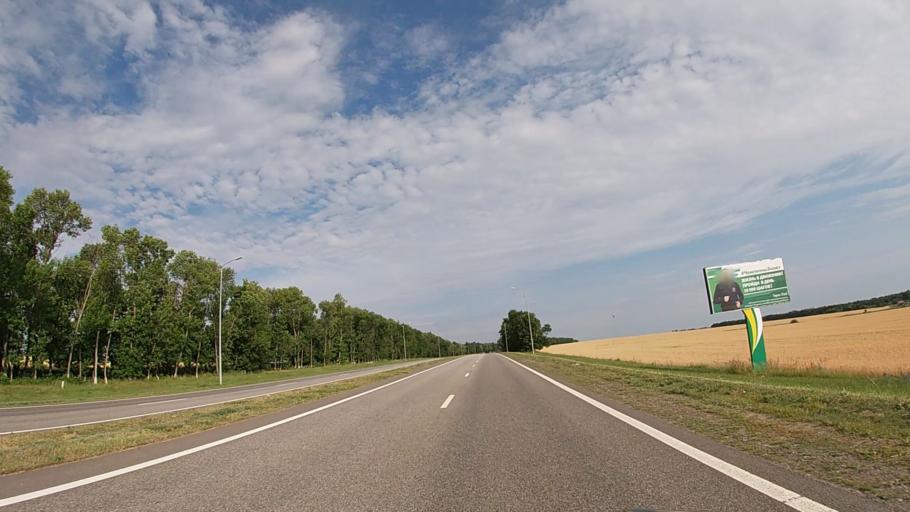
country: RU
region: Belgorod
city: Tomarovka
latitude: 50.6701
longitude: 36.3036
